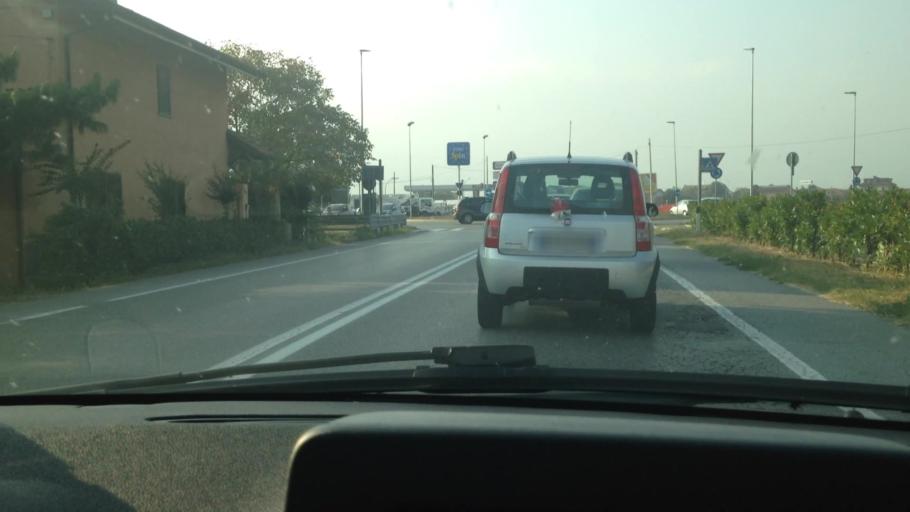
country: IT
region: Piedmont
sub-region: Provincia di Torino
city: San Maurizio
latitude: 45.1936
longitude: 7.6285
